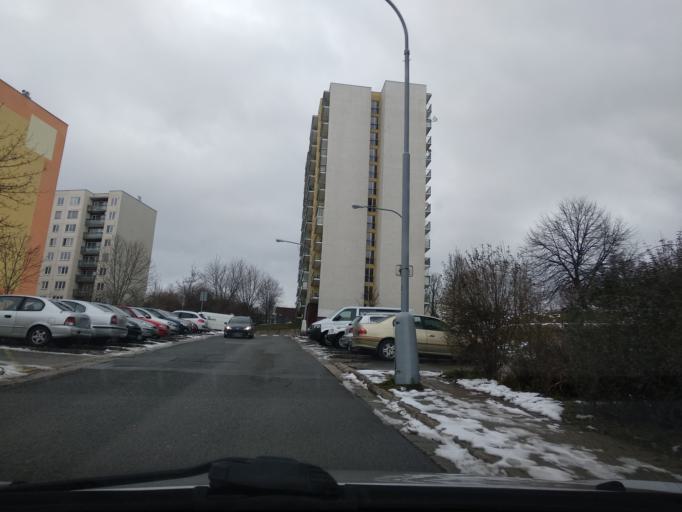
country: CZ
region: South Moravian
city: Ostopovice
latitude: 49.1751
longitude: 16.5581
